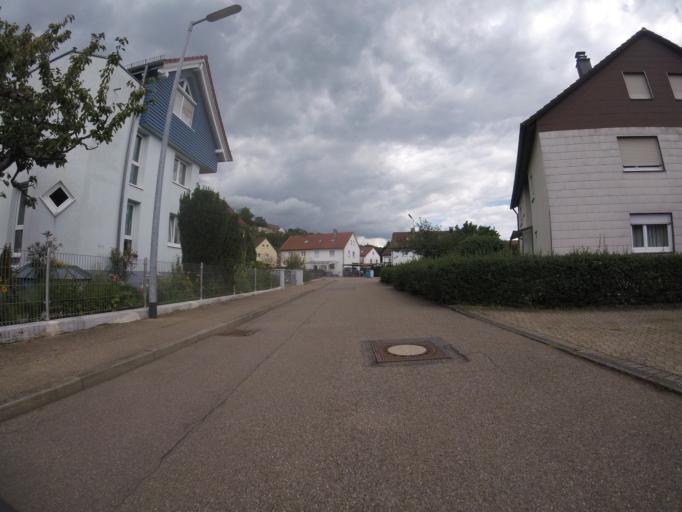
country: DE
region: Baden-Wuerttemberg
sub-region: Regierungsbezirk Stuttgart
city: Lorch
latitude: 48.7957
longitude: 9.7002
